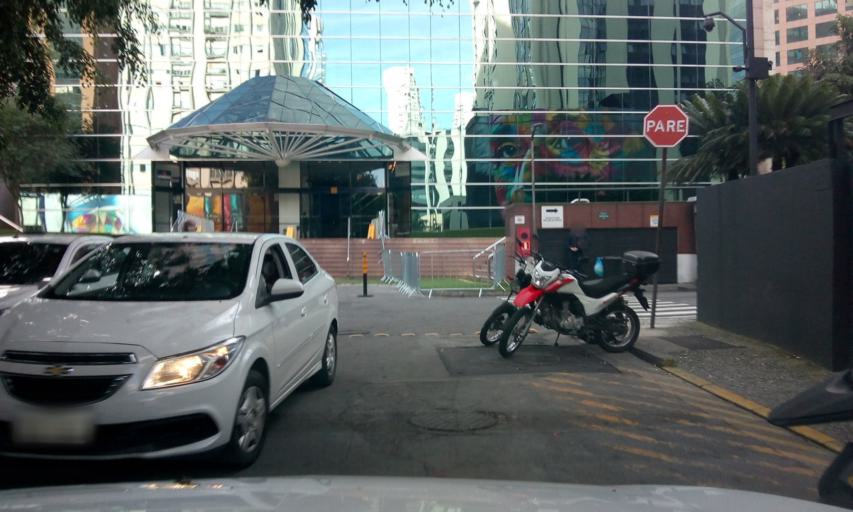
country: BR
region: Sao Paulo
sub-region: Sao Paulo
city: Sao Paulo
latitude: -23.6093
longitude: -46.6953
